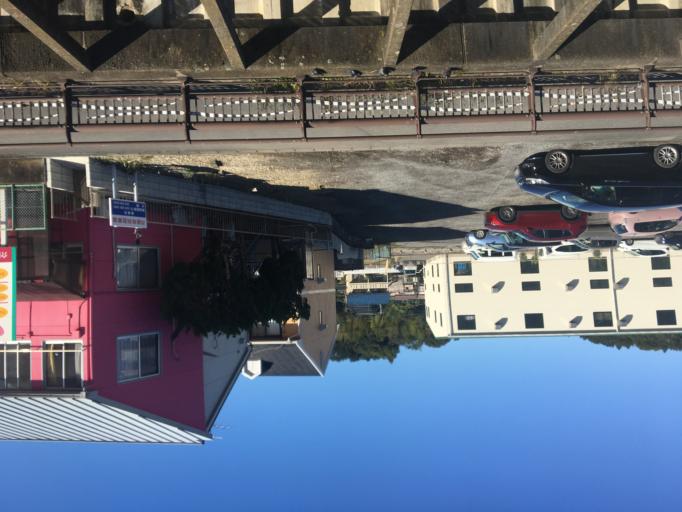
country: JP
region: Chiba
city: Sakura
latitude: 35.7255
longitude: 140.2255
